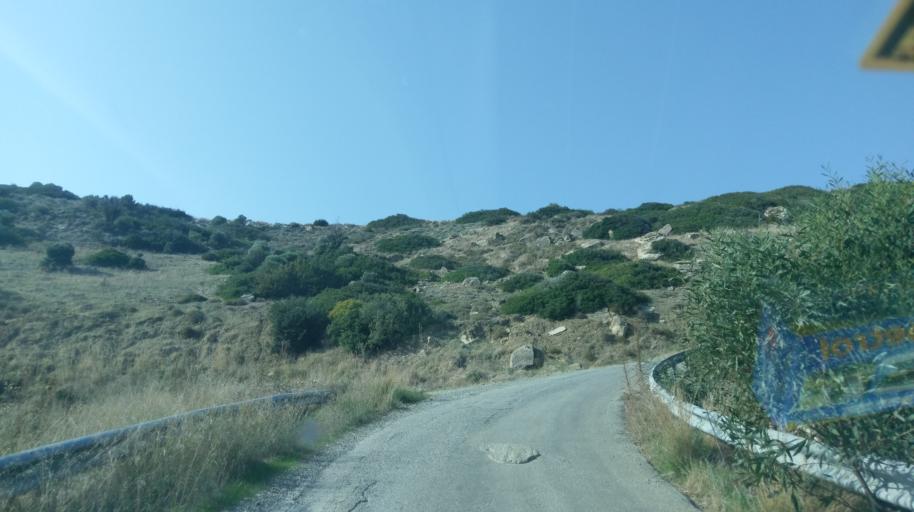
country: CY
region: Lefkosia
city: Morfou
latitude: 35.3657
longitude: 32.9937
